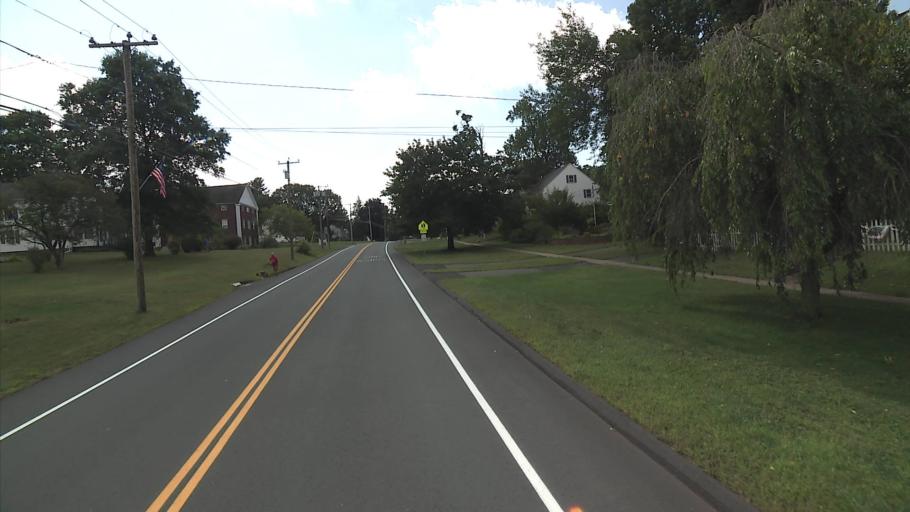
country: US
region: Connecticut
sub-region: Middlesex County
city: Cromwell
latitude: 41.5941
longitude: -72.6221
